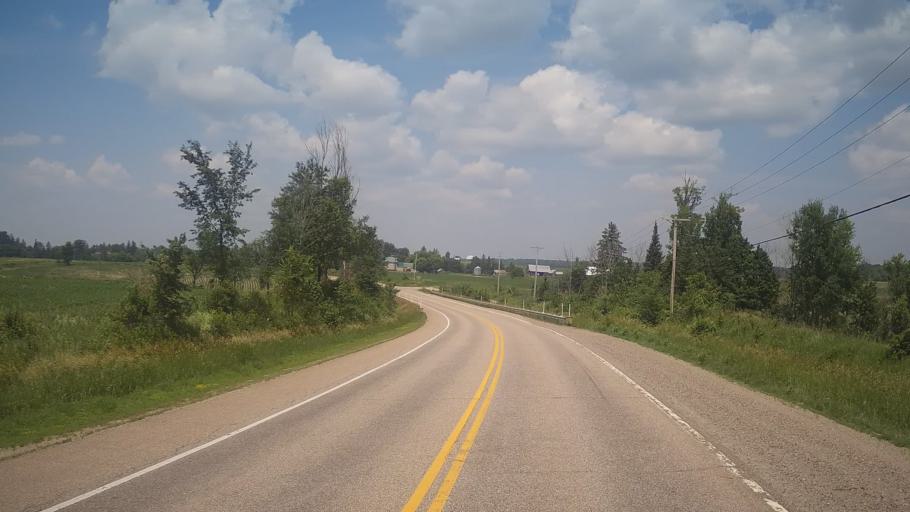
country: CA
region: Quebec
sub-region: Outaouais
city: Shawville
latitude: 45.5828
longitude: -76.4517
